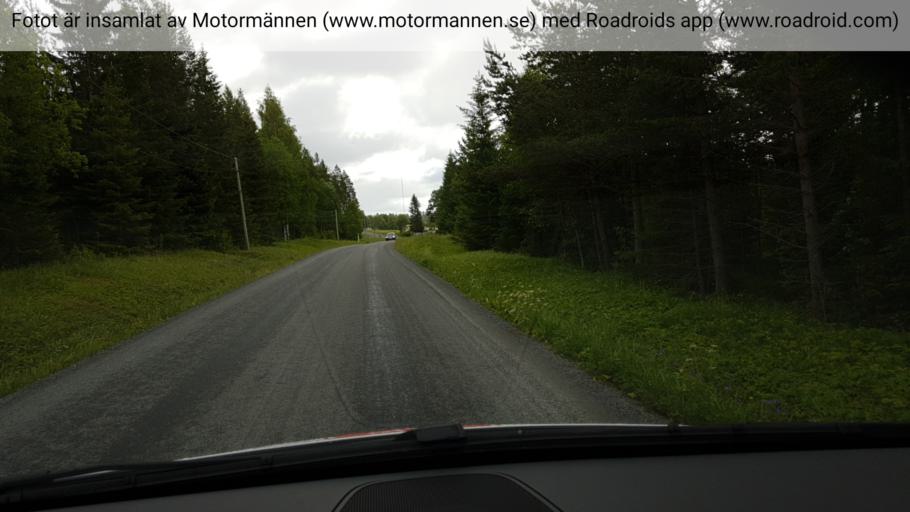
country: SE
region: Jaemtland
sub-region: OEstersunds Kommun
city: Ostersund
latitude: 63.1436
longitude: 14.5558
